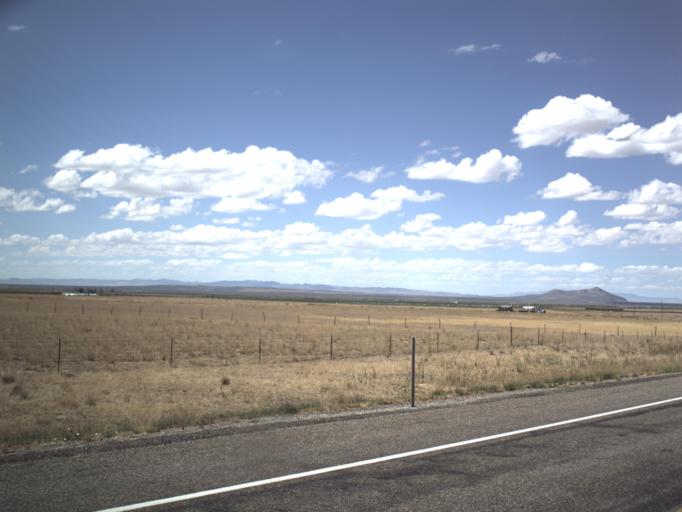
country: US
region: Utah
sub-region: Millard County
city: Fillmore
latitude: 39.1167
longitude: -112.3123
